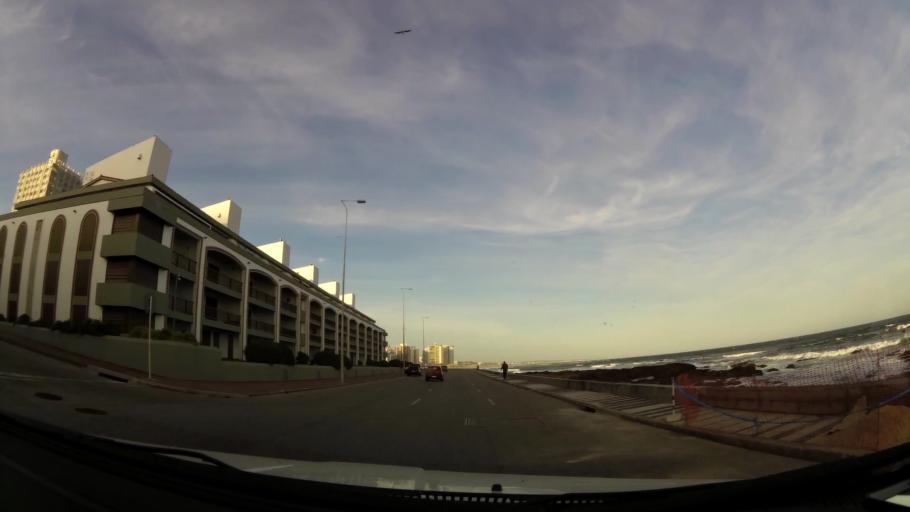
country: UY
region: Maldonado
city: Punta del Este
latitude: -34.9615
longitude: -54.9393
